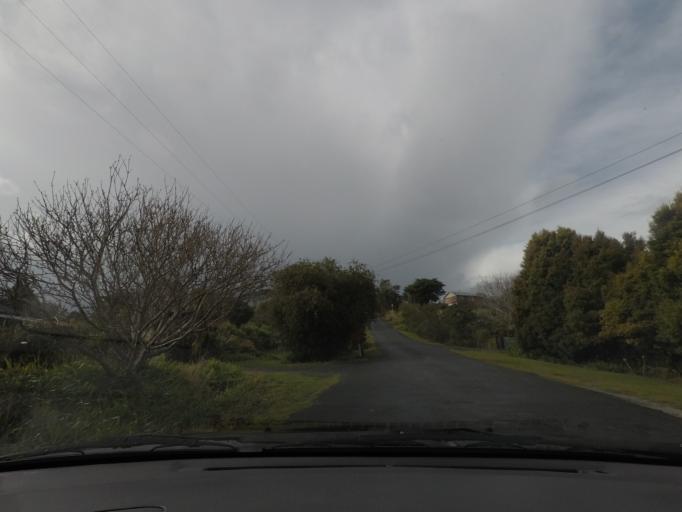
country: NZ
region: Auckland
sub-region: Auckland
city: Warkworth
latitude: -36.4716
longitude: 174.7327
